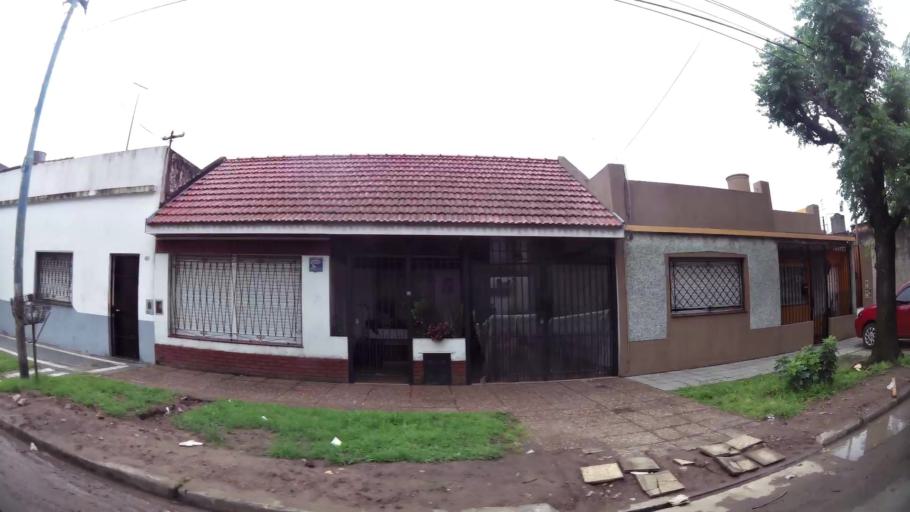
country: AR
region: Buenos Aires
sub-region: Partido de Lanus
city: Lanus
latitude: -34.7328
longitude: -58.3818
